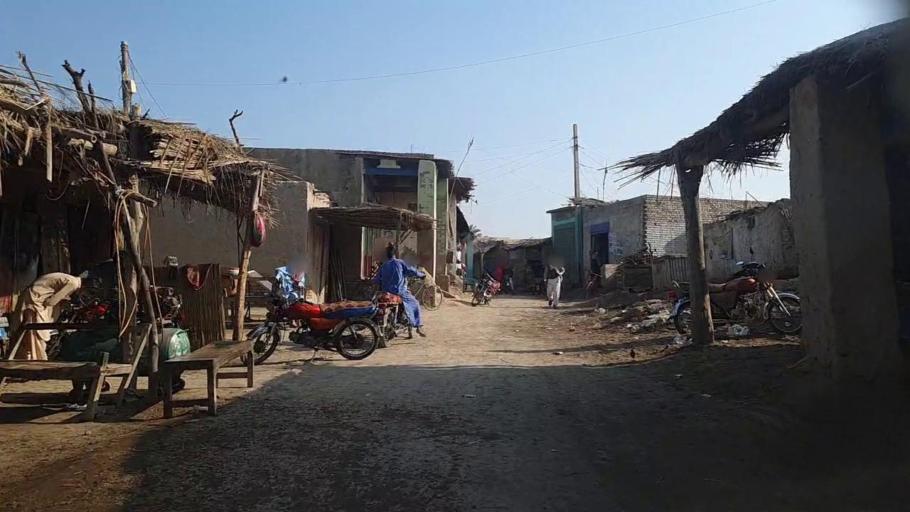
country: PK
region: Sindh
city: Mirpur Mathelo
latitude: 27.8902
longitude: 69.6062
